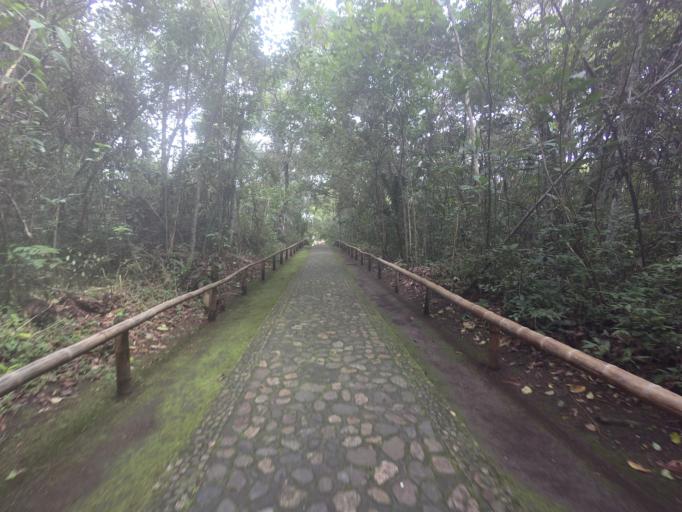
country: CO
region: Huila
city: San Agustin
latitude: 1.8847
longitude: -76.2955
